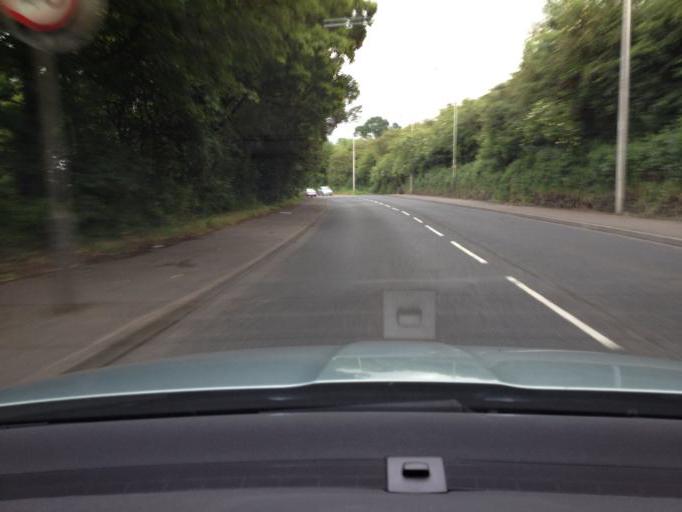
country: GB
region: Scotland
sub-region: Perth and Kinross
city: Perth
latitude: 56.3752
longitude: -3.4285
